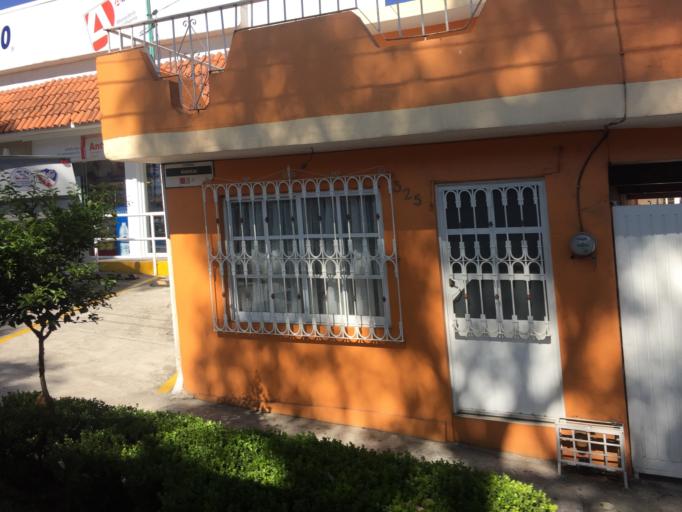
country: MX
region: Veracruz
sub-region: Xalapa
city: Xalapa de Enriquez
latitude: 19.5358
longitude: -96.9121
